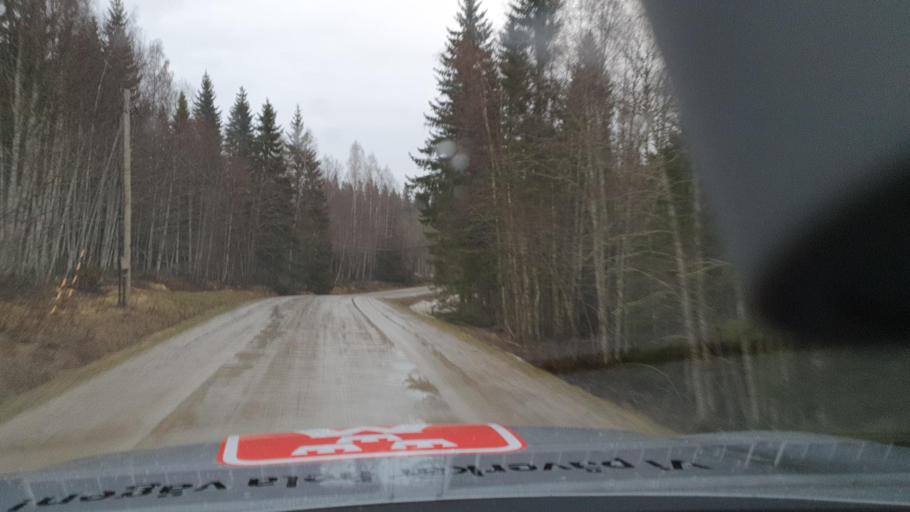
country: SE
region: Vaesternorrland
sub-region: OErnskoeldsviks Kommun
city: Bjasta
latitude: 63.2428
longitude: 18.3355
